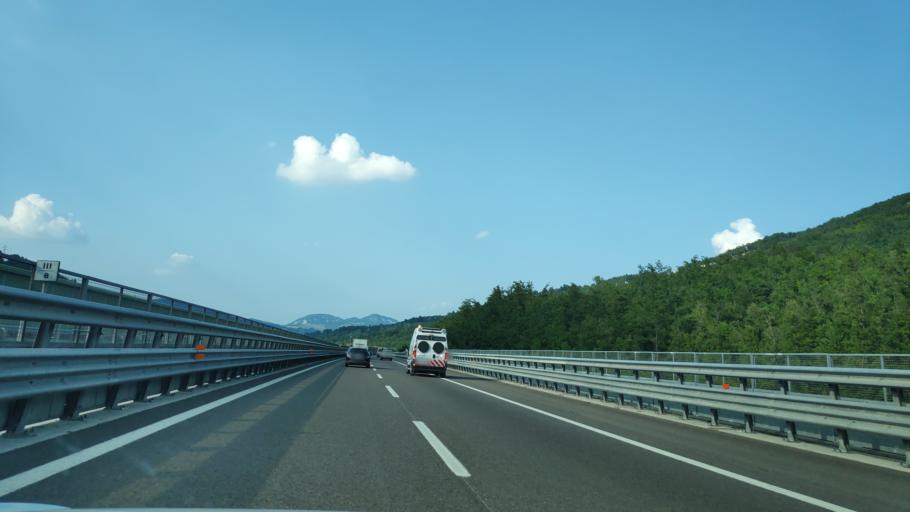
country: IT
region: Emilia-Romagna
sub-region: Provincia di Bologna
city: Grizzana
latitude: 44.2337
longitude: 11.1845
